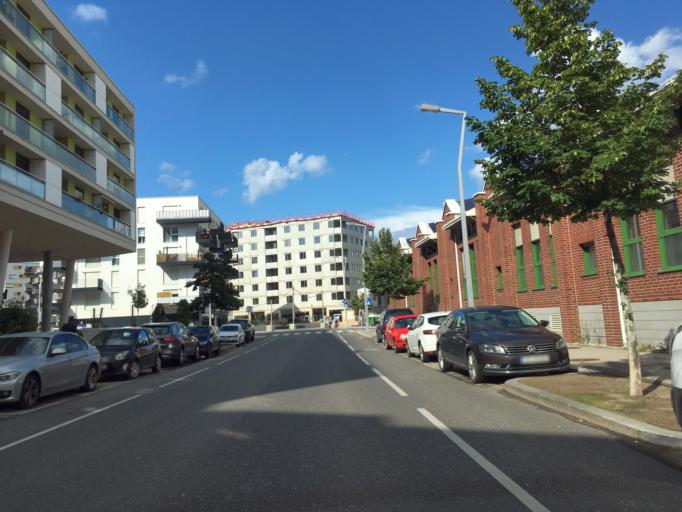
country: AT
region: Lower Austria
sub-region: Politischer Bezirk Wien-Umgebung
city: Gerasdorf bei Wien
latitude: 48.2294
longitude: 16.4590
